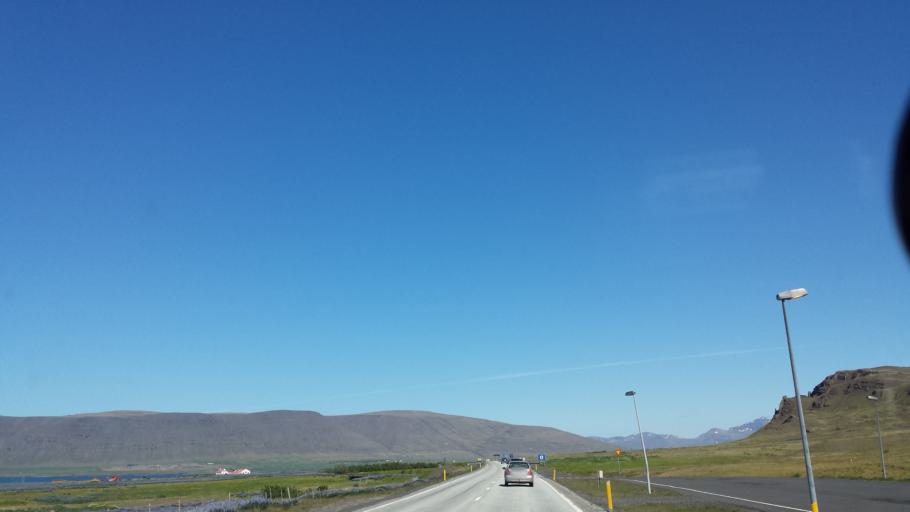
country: IS
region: Capital Region
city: Reykjavik
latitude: 64.2659
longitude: -21.8338
